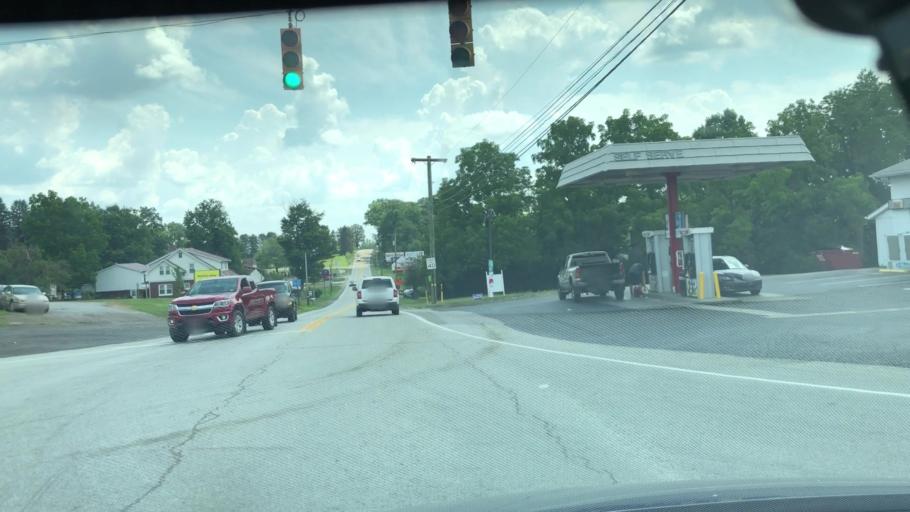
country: US
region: Pennsylvania
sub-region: Butler County
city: Saxonburg
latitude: 40.7601
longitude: -79.7789
